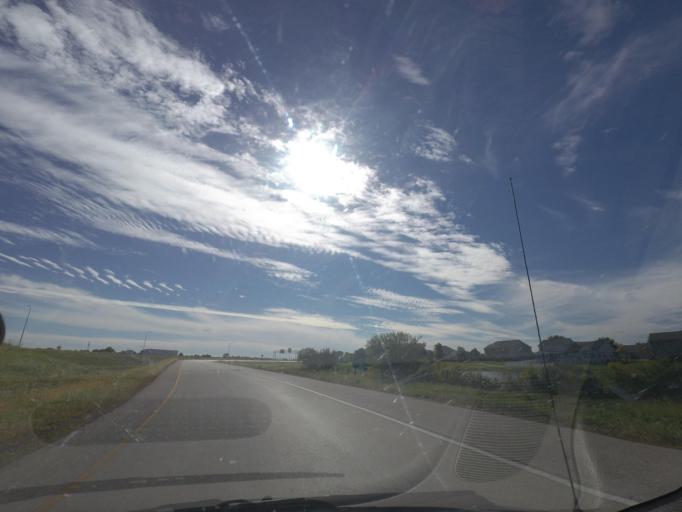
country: US
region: Illinois
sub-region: Champaign County
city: Champaign
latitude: 40.1215
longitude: -88.3071
